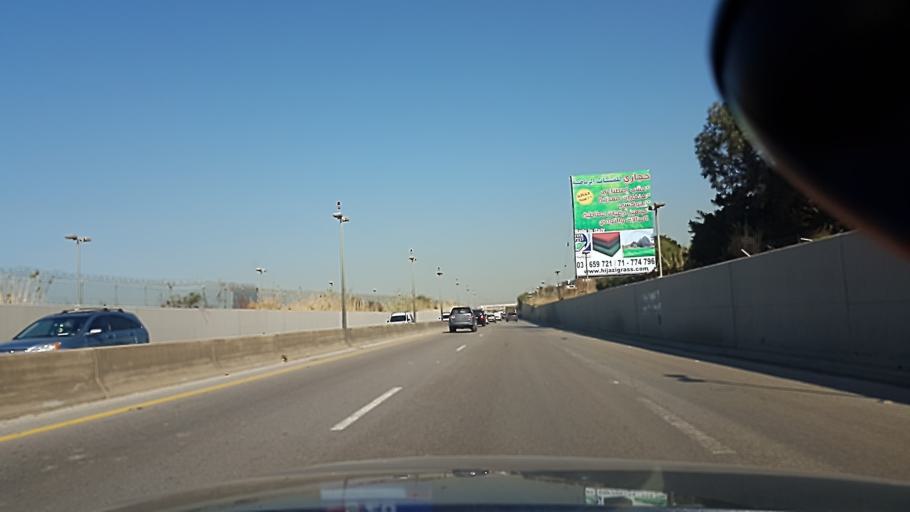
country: LB
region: Mont-Liban
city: Baabda
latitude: 33.7984
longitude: 35.4834
